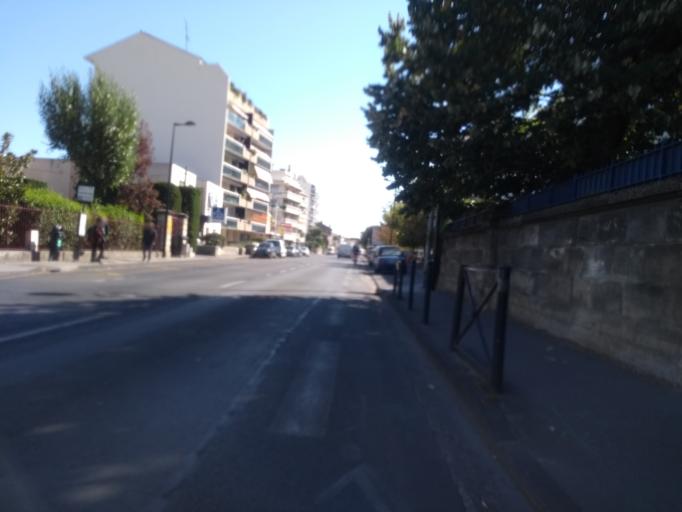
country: FR
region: Aquitaine
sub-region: Departement de la Gironde
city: Le Bouscat
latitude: 44.8541
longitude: -0.6116
